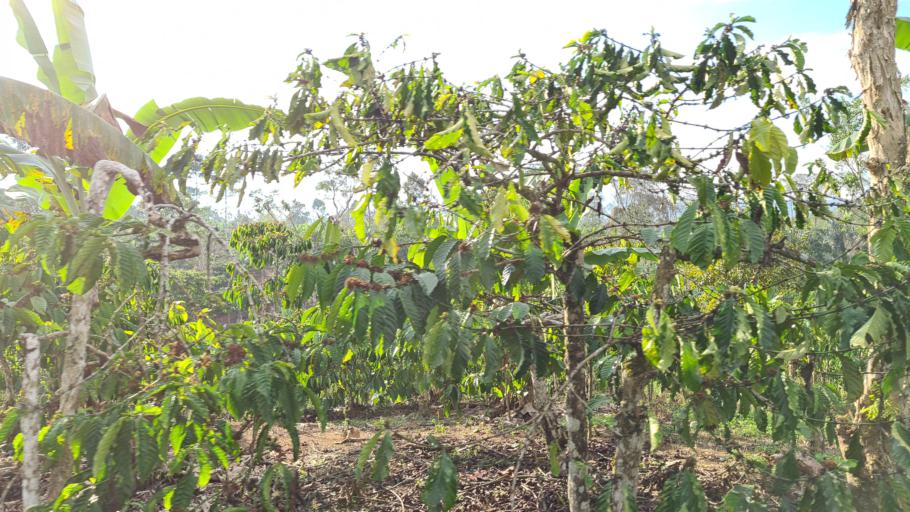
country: ID
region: Lampung
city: Kenali
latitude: -5.0816
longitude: 104.4072
